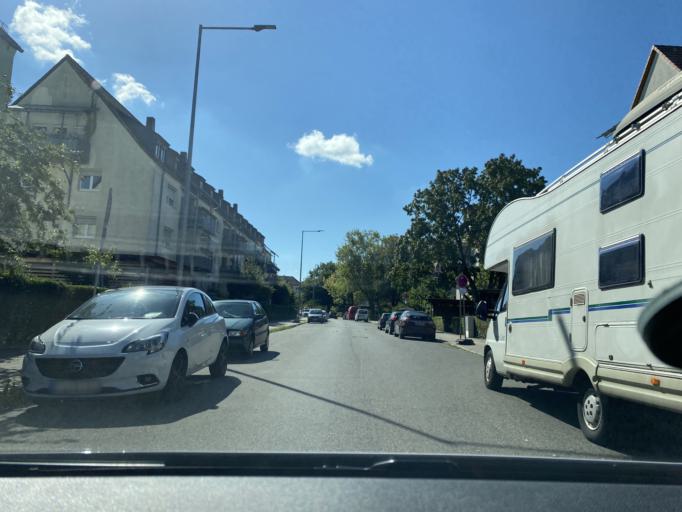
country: DE
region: Bavaria
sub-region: Regierungsbezirk Mittelfranken
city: Furth
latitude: 49.4542
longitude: 10.9915
